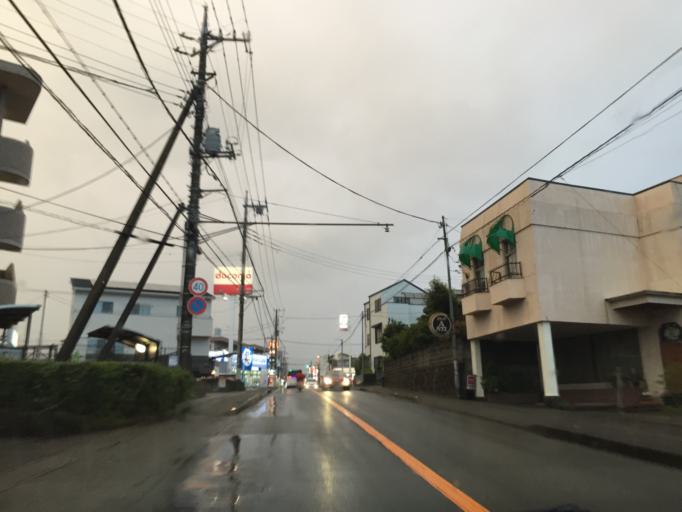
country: JP
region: Shizuoka
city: Mishima
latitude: 35.1445
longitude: 138.9104
